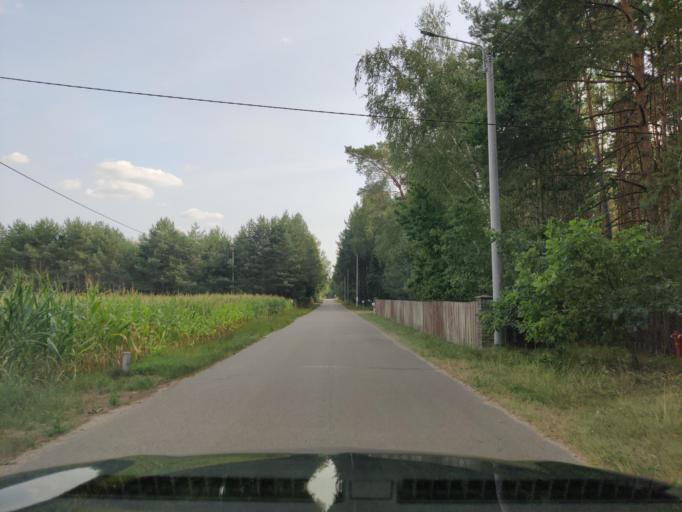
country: PL
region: Masovian Voivodeship
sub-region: Powiat makowski
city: Rozan
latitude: 52.8576
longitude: 21.4516
